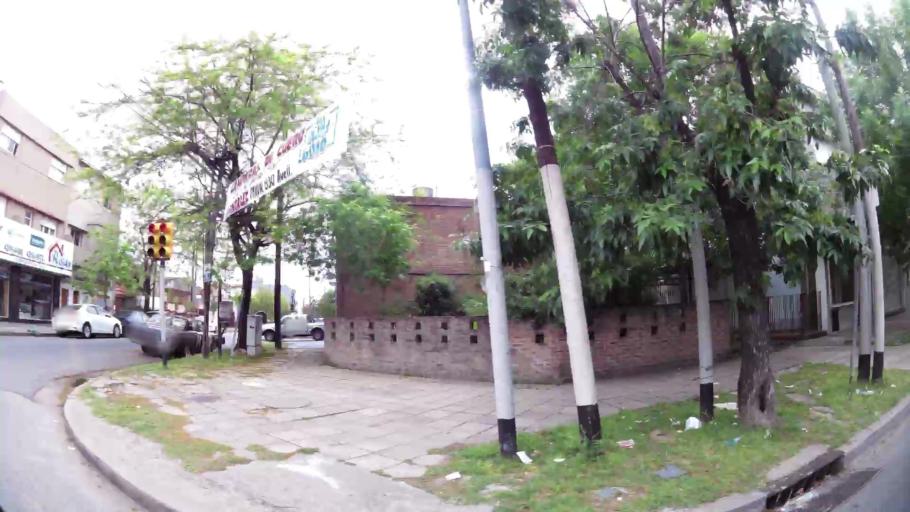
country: AR
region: Buenos Aires
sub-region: Partido de Lanus
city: Lanus
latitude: -34.6841
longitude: -58.3952
